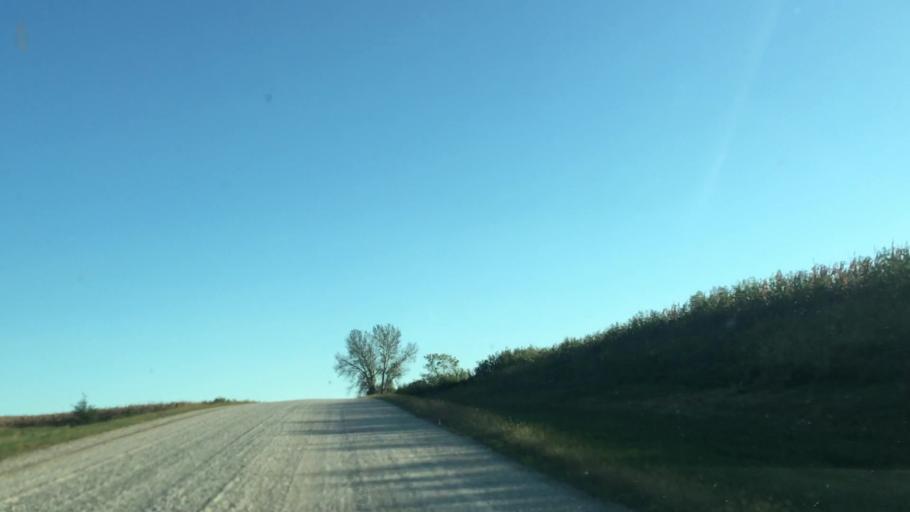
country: US
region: Minnesota
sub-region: Fillmore County
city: Preston
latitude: 43.8045
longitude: -92.0395
